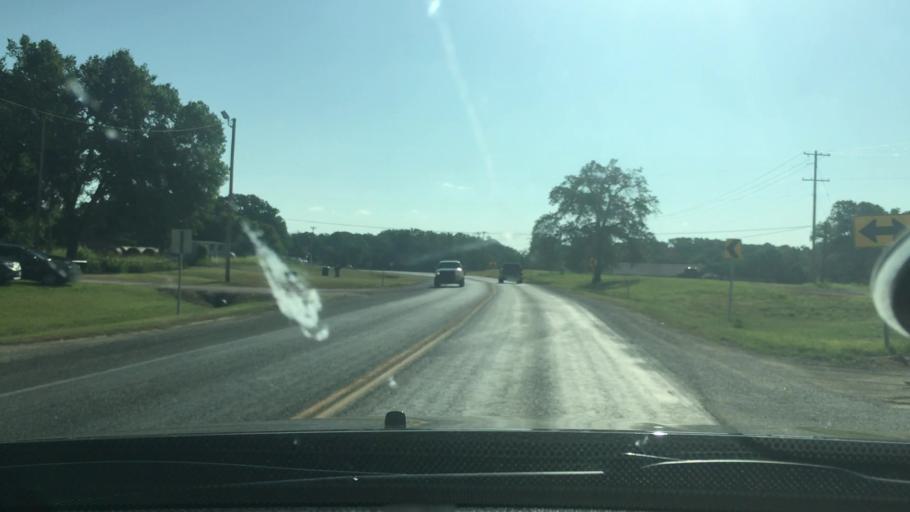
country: US
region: Oklahoma
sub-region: Johnston County
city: Tishomingo
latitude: 34.2372
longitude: -96.6998
